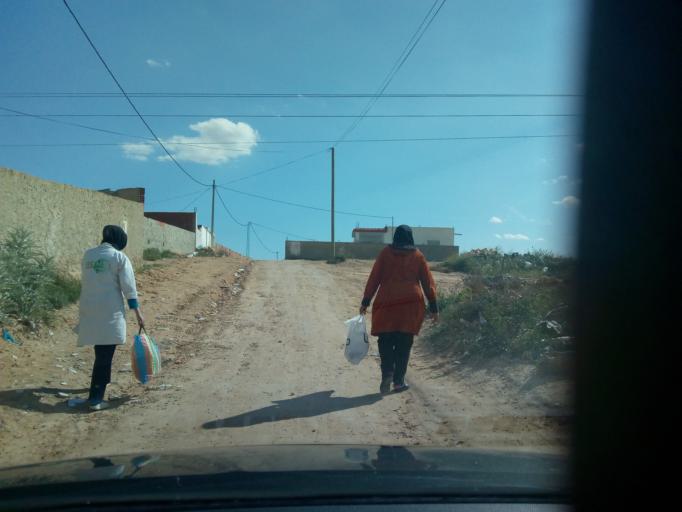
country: TN
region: Safaqis
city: Sfax
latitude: 34.7303
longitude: 10.6048
